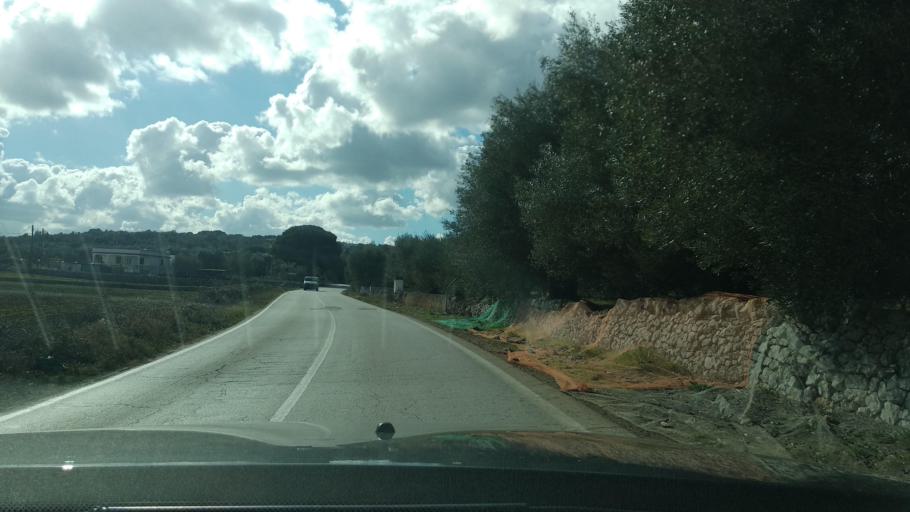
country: IT
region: Apulia
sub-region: Provincia di Brindisi
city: Casalini
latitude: 40.7040
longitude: 17.4998
